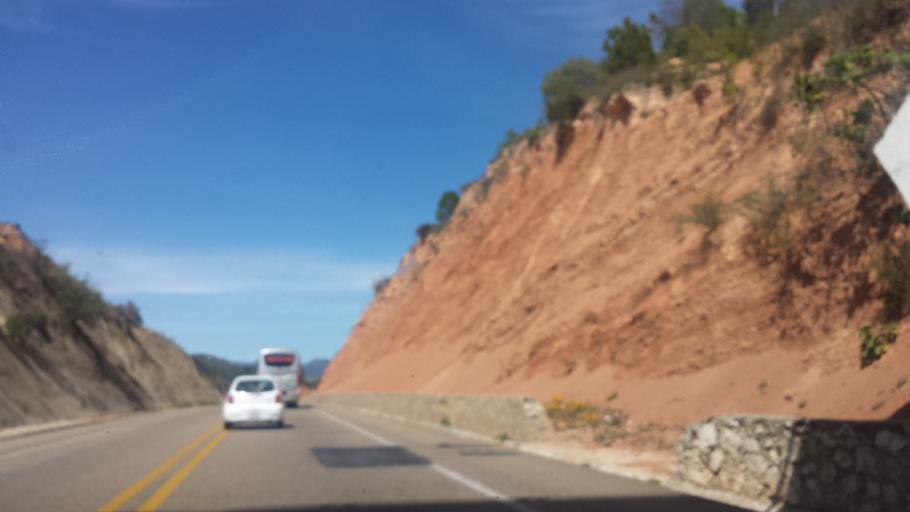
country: MX
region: Oaxaca
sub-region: Villa Tejupam de la Union
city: Villa Tejupam de la Union
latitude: 17.6634
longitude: -97.3497
